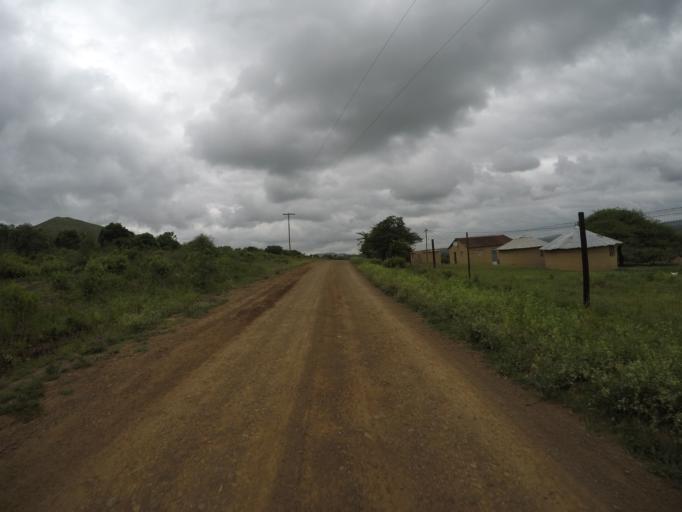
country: ZA
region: KwaZulu-Natal
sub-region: uThungulu District Municipality
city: Empangeni
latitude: -28.5715
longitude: 31.8731
